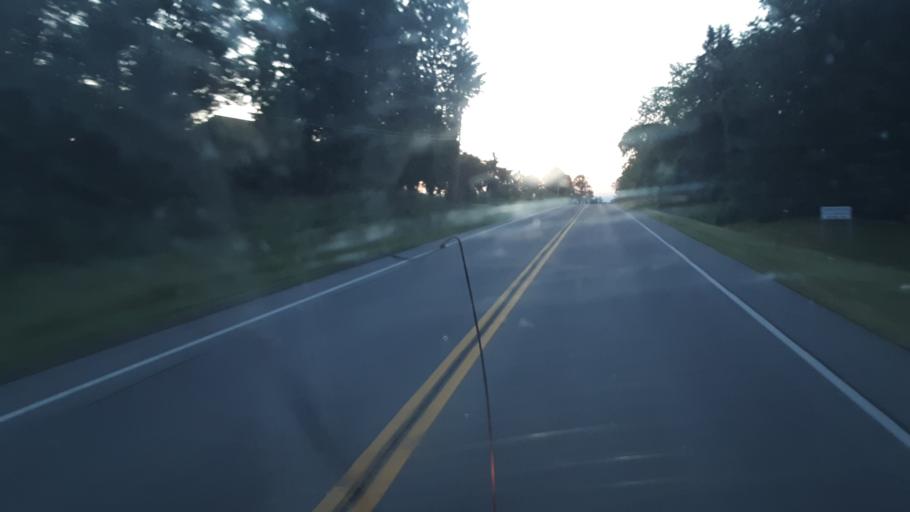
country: US
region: New York
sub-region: Schenectady County
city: East Glenville
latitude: 42.9752
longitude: -73.9979
